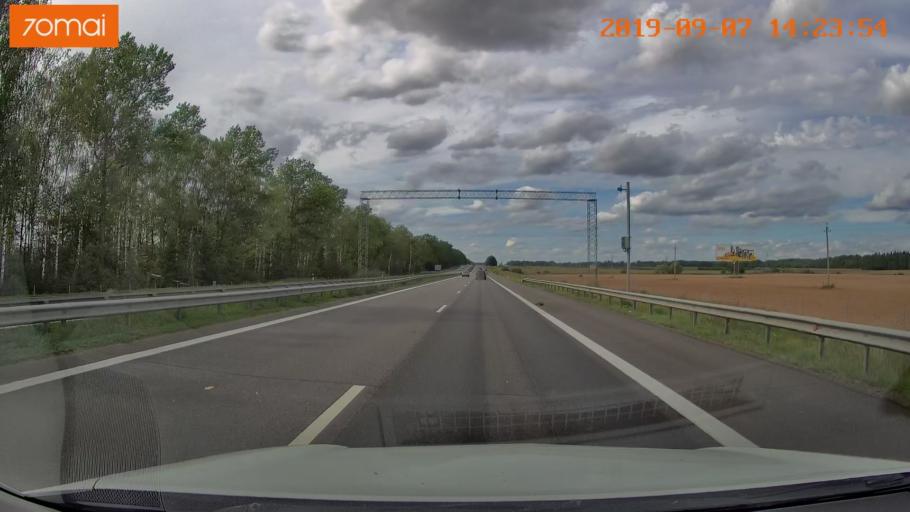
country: LT
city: Ziezmariai
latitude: 54.8216
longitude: 24.4131
